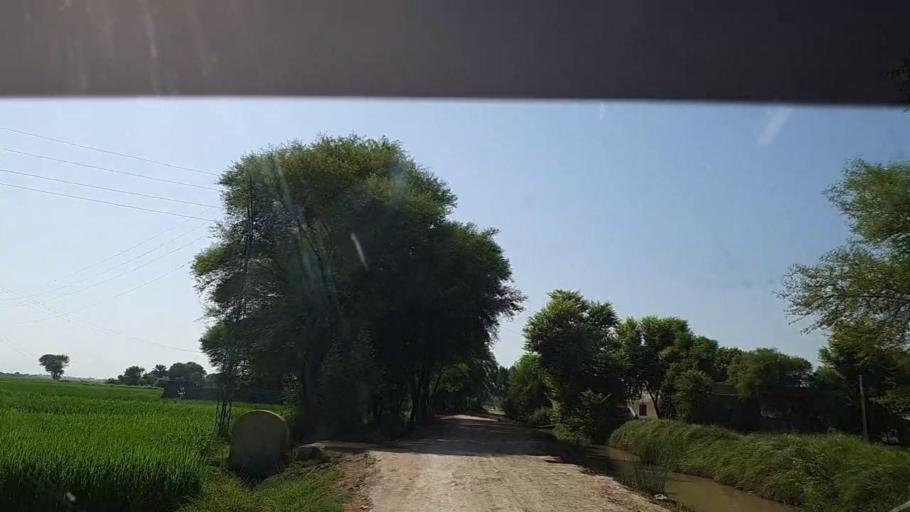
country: PK
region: Sindh
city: Ghauspur
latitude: 28.1724
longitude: 69.0578
